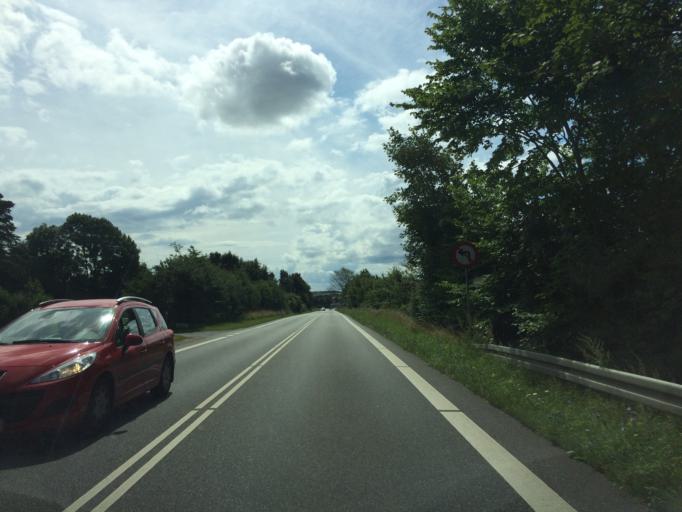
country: DK
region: South Denmark
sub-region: Faaborg-Midtfyn Kommune
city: Faaborg
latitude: 55.1168
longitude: 10.2447
